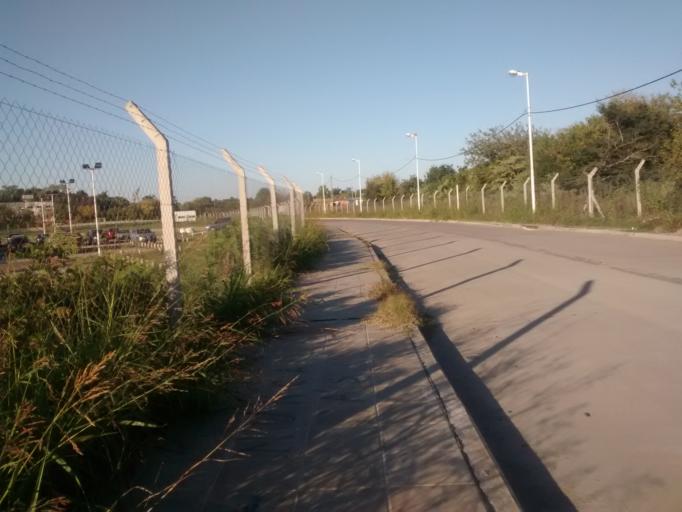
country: AR
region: Buenos Aires
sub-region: Partido de La Plata
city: La Plata
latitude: -34.9017
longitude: -57.9313
